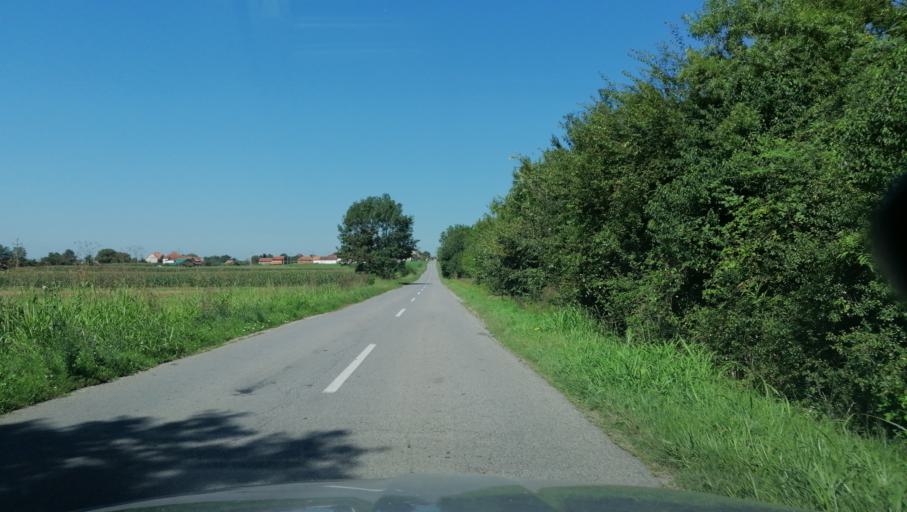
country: RS
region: Central Serbia
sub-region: Raski Okrug
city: Vrnjacka Banja
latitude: 43.6844
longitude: 20.8840
